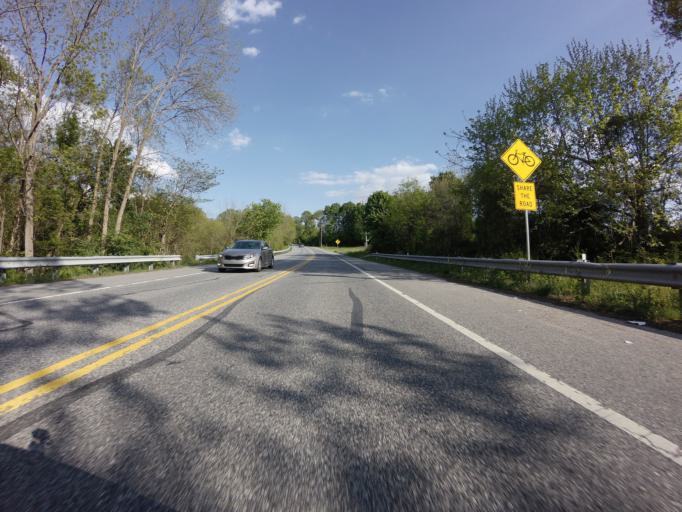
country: US
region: Maryland
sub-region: Baltimore County
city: Hunt Valley
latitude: 39.5288
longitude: -76.7246
